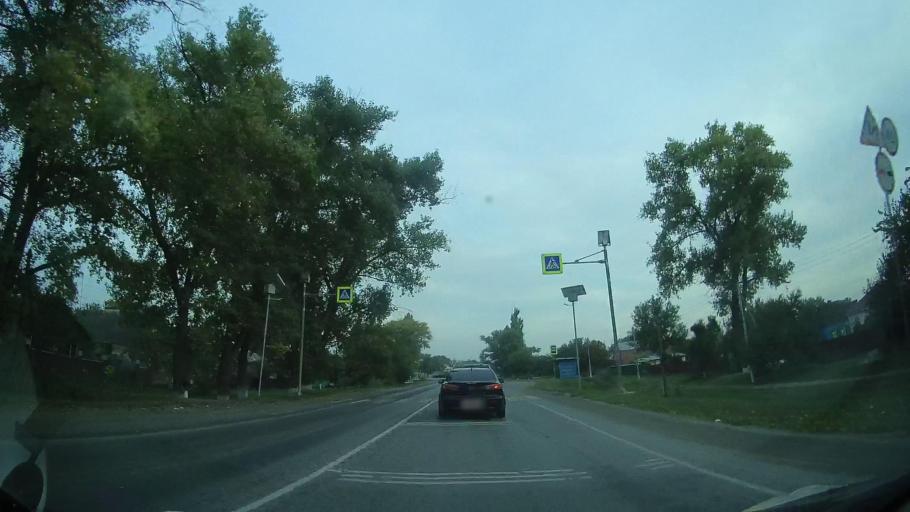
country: RU
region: Rostov
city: Kirovskaya
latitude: 46.9831
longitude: 40.0336
